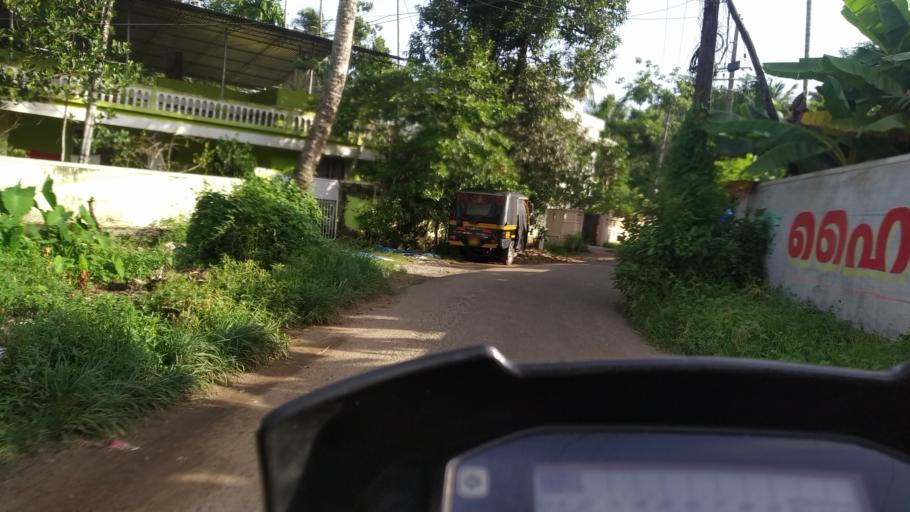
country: IN
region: Kerala
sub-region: Thrissur District
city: Kodungallur
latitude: 10.1339
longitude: 76.1921
